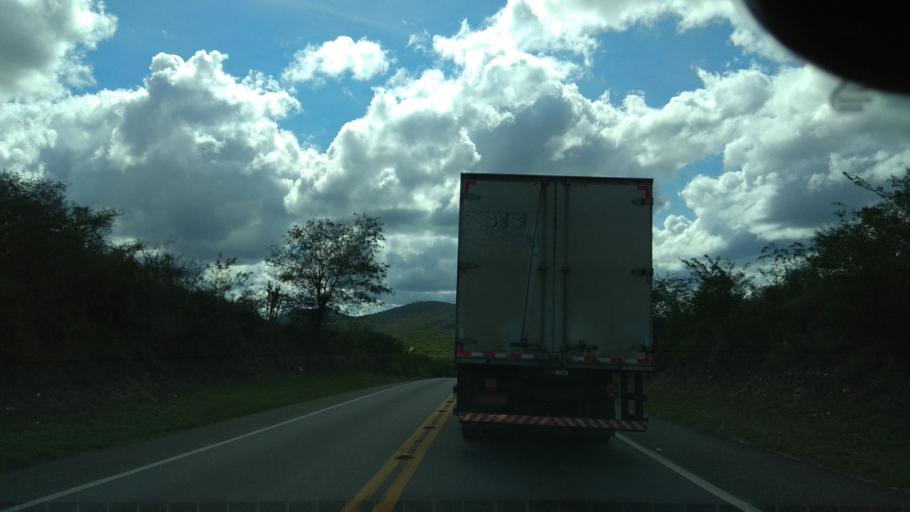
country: BR
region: Bahia
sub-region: Jequie
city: Jequie
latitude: -13.7425
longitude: -40.0986
